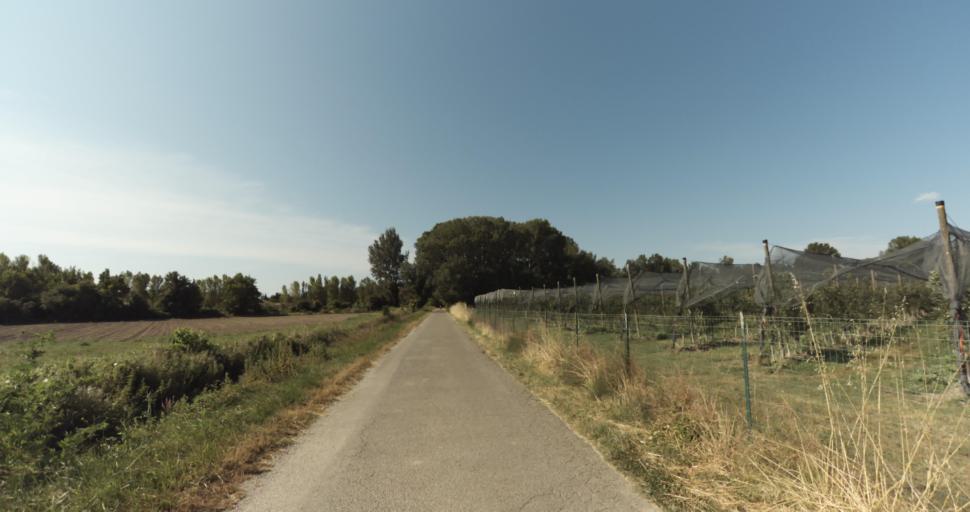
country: FR
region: Provence-Alpes-Cote d'Azur
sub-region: Departement du Vaucluse
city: Althen-des-Paluds
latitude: 44.0078
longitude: 4.9739
